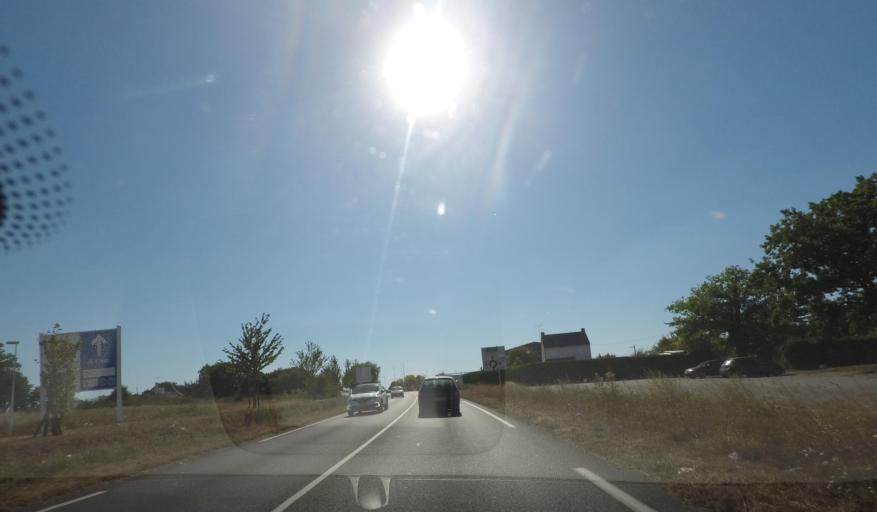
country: FR
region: Pays de la Loire
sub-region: Departement de la Loire-Atlantique
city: Pontchateau
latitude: 47.4365
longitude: -2.0790
